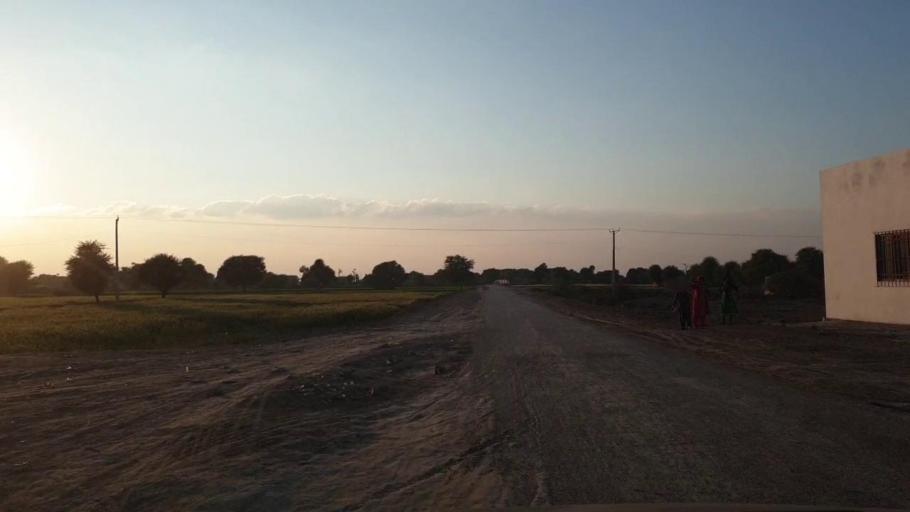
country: PK
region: Sindh
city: Shahpur Chakar
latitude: 26.1581
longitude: 68.5436
